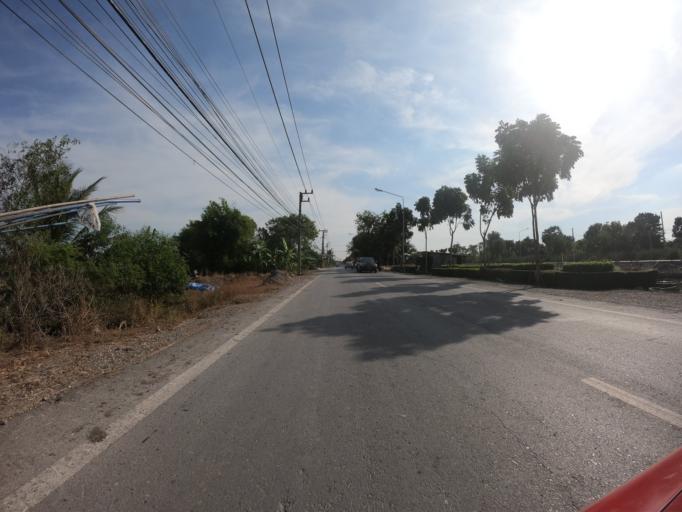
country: TH
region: Pathum Thani
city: Thanyaburi
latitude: 14.0013
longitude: 100.7308
